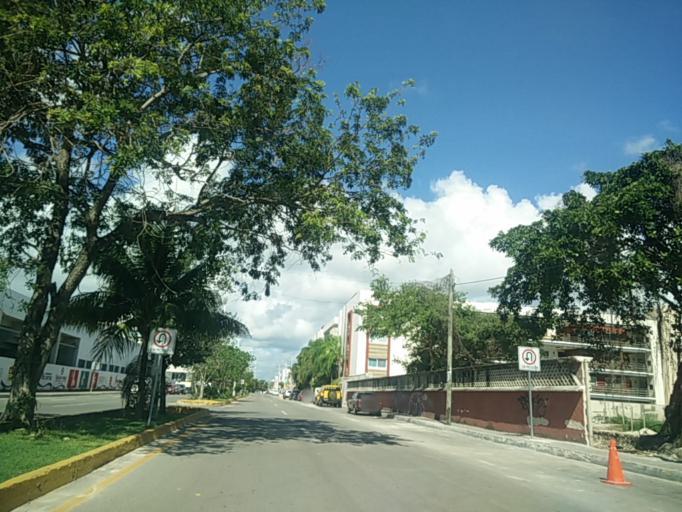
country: MX
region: Quintana Roo
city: Playa del Carmen
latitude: 20.6349
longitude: -87.0687
